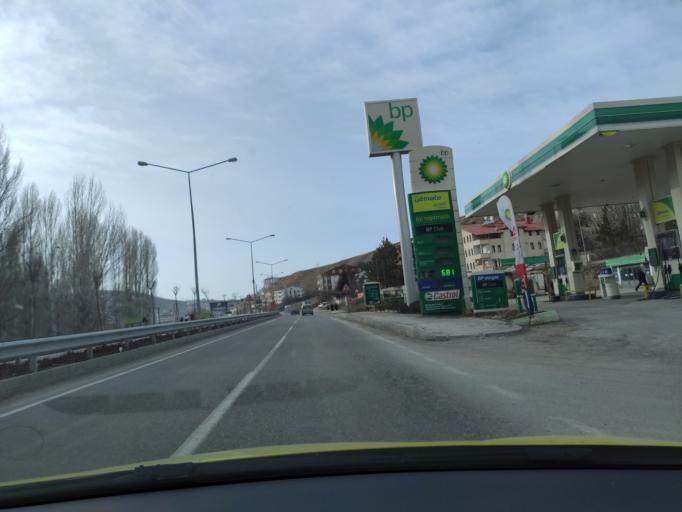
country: TR
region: Bayburt
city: Bayburt
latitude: 40.2421
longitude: 40.2447
